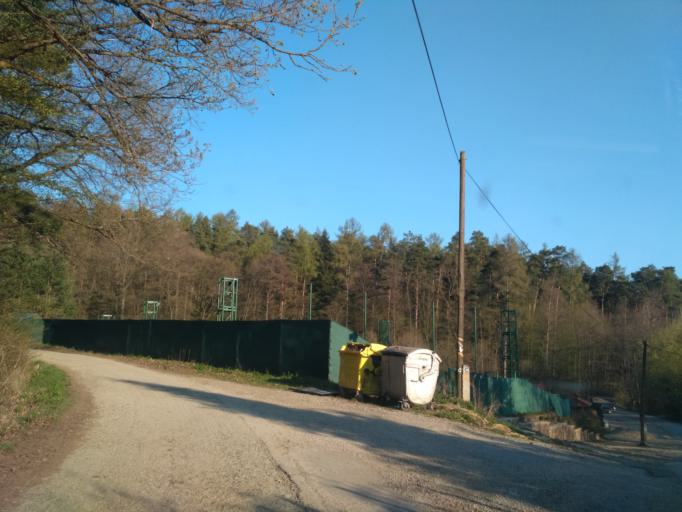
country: SK
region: Kosicky
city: Kosice
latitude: 48.7332
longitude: 21.1613
